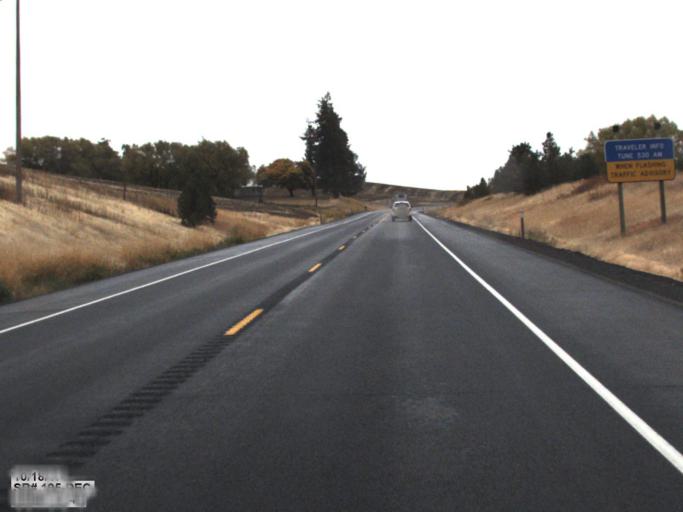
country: US
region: Washington
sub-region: Whitman County
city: Pullman
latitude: 46.7499
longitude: -117.2359
